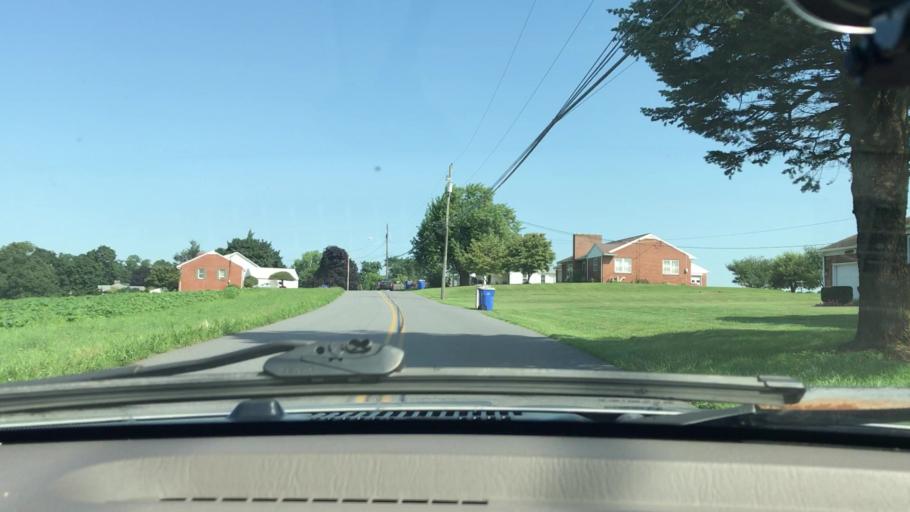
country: US
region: Pennsylvania
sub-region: Dauphin County
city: Rutherford
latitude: 40.2516
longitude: -76.7408
